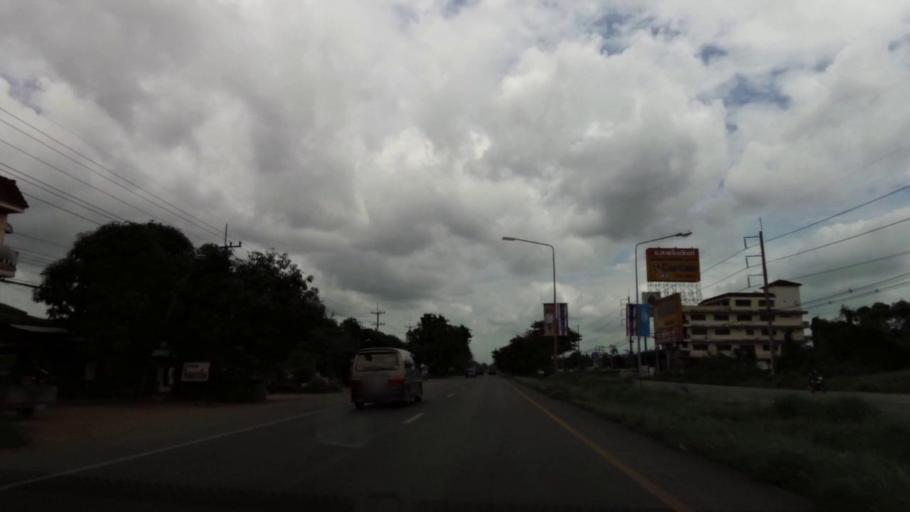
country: TH
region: Rayong
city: Klaeng
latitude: 12.7821
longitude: 101.6924
